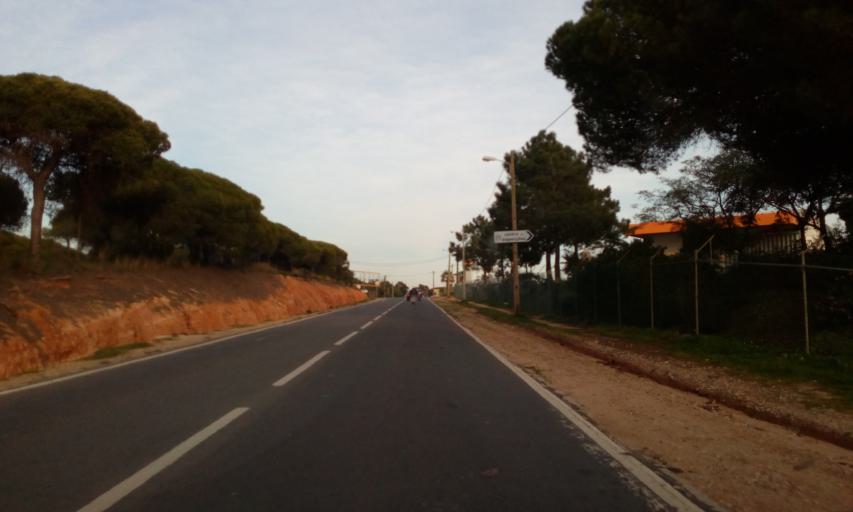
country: PT
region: Faro
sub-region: Faro
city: Faro
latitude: 37.0218
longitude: -7.9776
